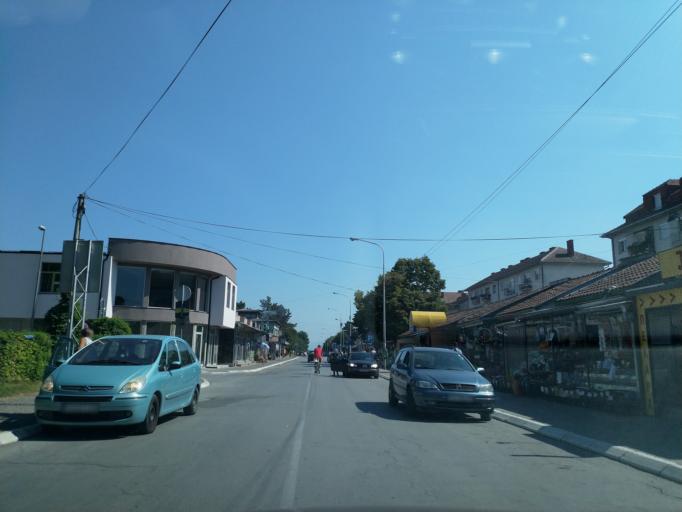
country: RS
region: Central Serbia
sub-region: Rasinski Okrug
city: Trstenik
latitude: 43.6185
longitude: 21.0052
